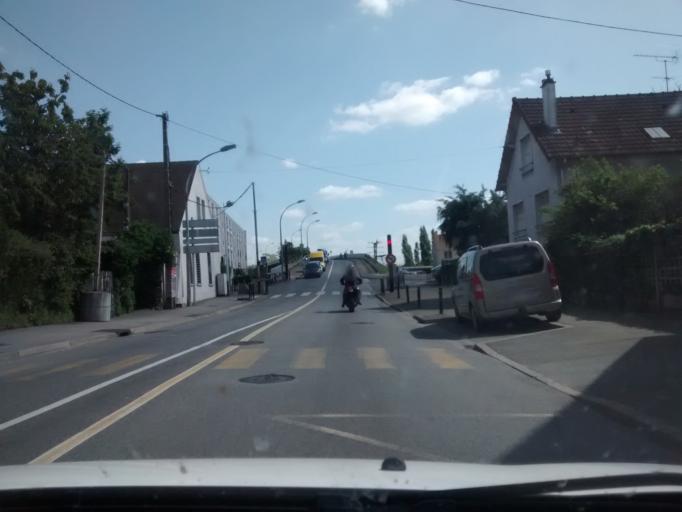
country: FR
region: Ile-de-France
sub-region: Departement des Yvelines
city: Trappes
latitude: 48.7747
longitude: 1.9993
